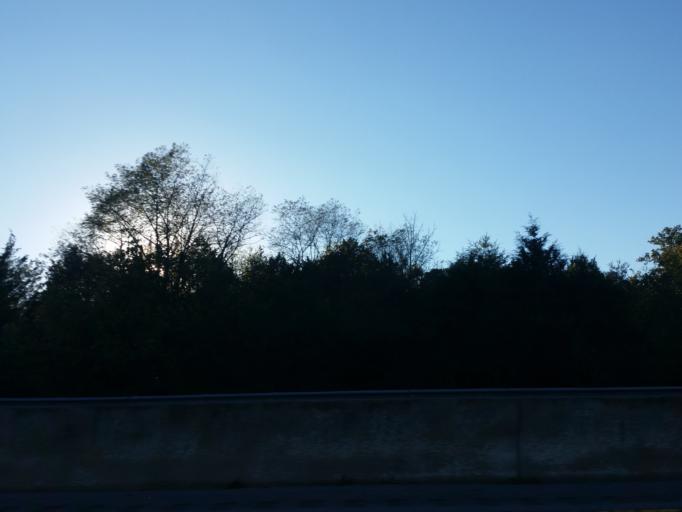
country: US
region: Tennessee
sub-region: Grainger County
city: Rutledge
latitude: 36.3530
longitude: -83.4351
